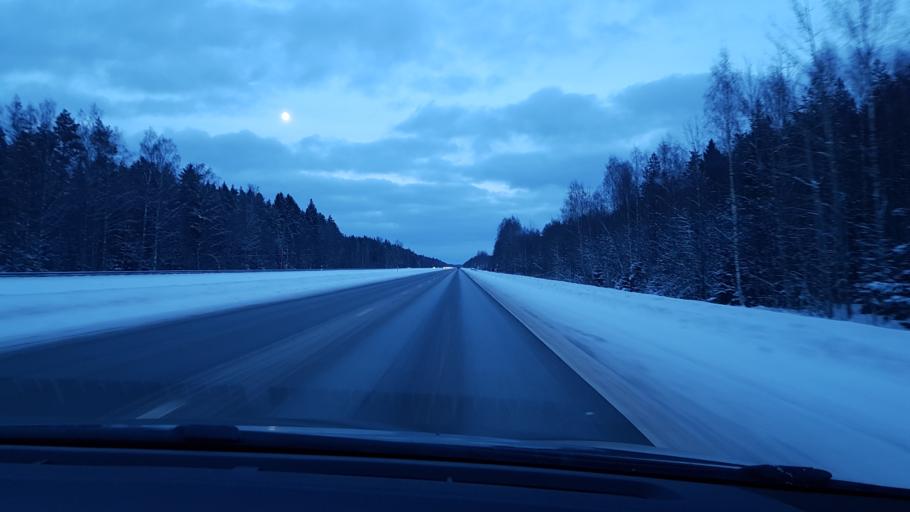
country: EE
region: Harju
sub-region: Kuusalu vald
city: Kuusalu
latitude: 59.4576
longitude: 25.5434
